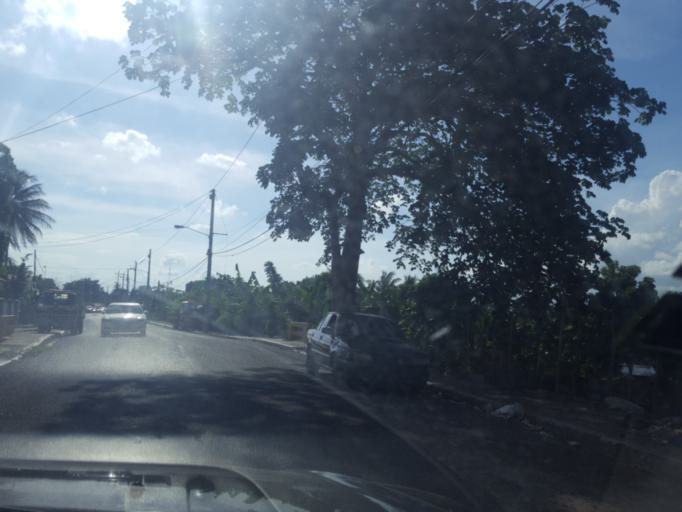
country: DO
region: Santiago
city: Licey al Medio
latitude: 19.3794
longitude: -70.6130
